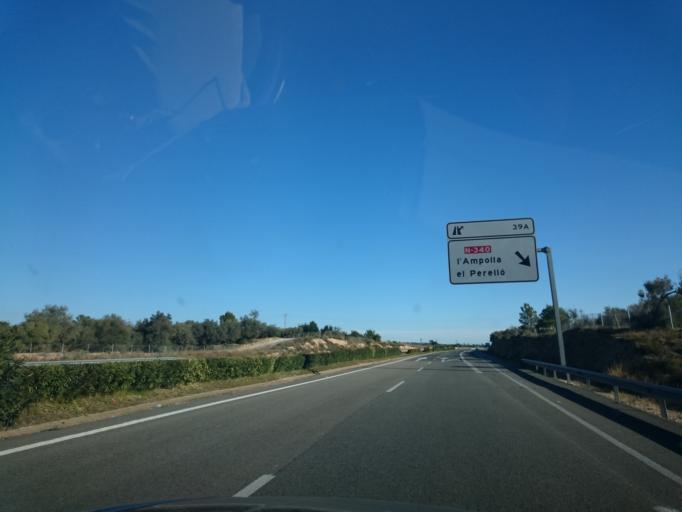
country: ES
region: Catalonia
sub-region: Provincia de Tarragona
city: L'Ampolla
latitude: 40.8093
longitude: 0.6981
